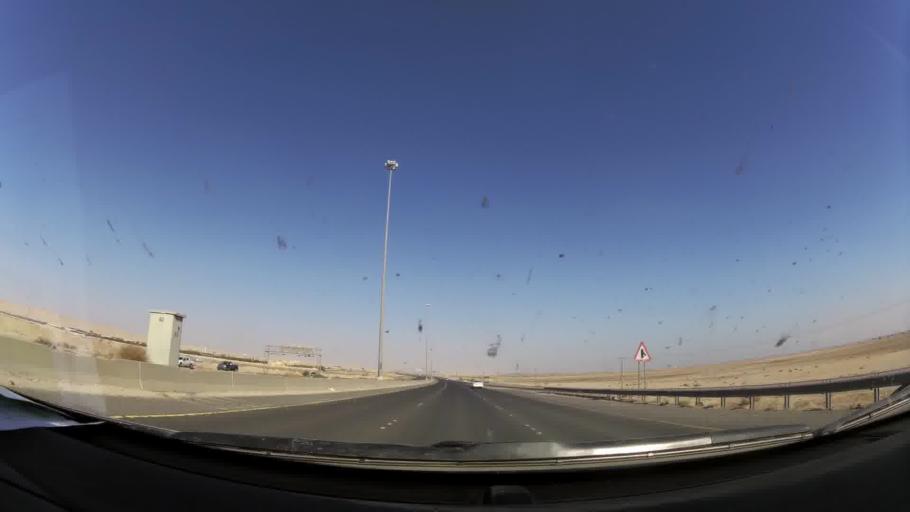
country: KW
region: Muhafazat al Jahra'
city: Al Jahra'
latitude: 29.3775
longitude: 47.6673
